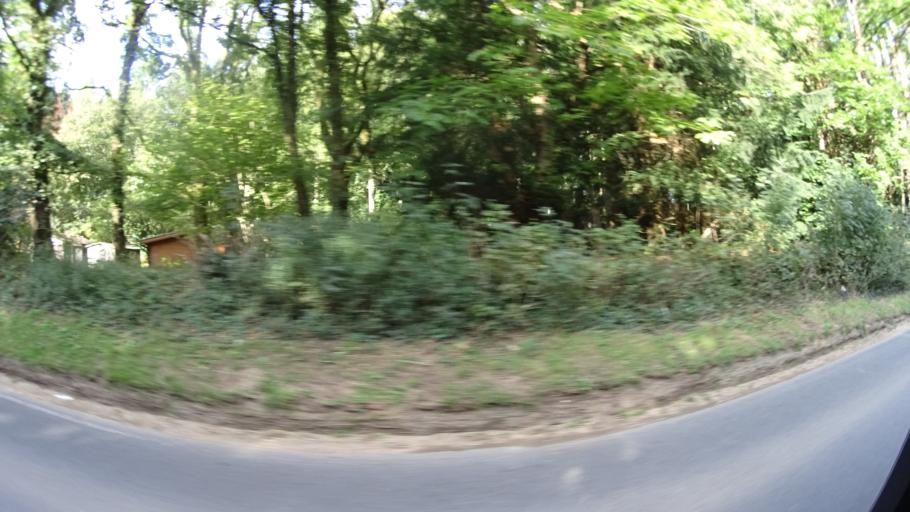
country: GB
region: England
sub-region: Dorset
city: Lytchett Matravers
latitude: 50.7815
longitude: -2.0725
